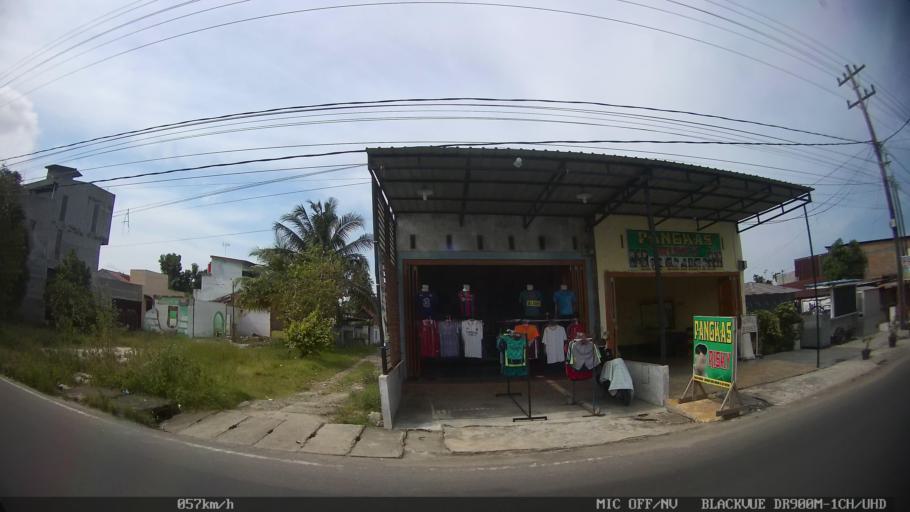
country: ID
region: North Sumatra
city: Percut
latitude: 3.6072
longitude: 98.7752
